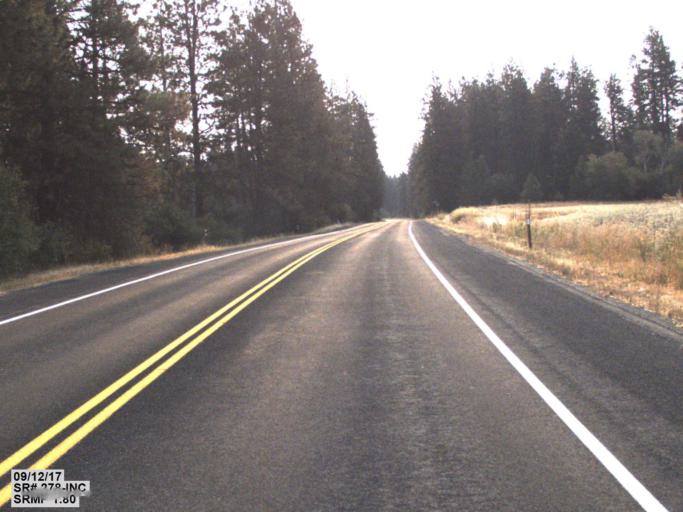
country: US
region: Washington
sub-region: Spokane County
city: Veradale
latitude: 47.4433
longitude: -117.1121
